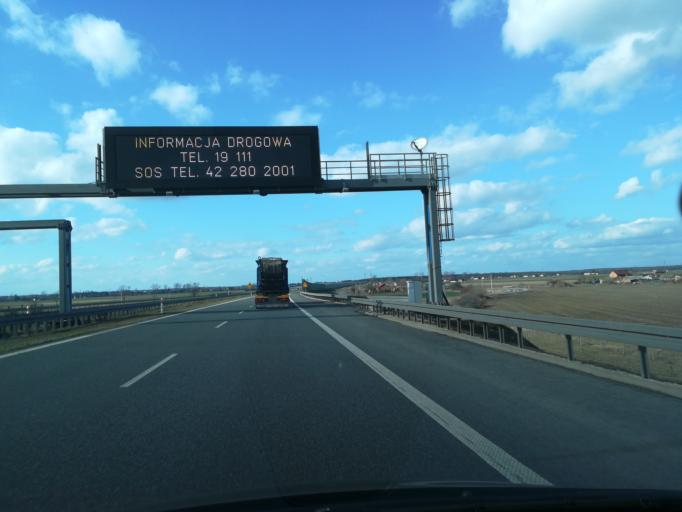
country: PL
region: Lodz Voivodeship
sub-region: Powiat kutnowski
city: Krzyzanow
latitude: 52.2323
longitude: 19.4569
